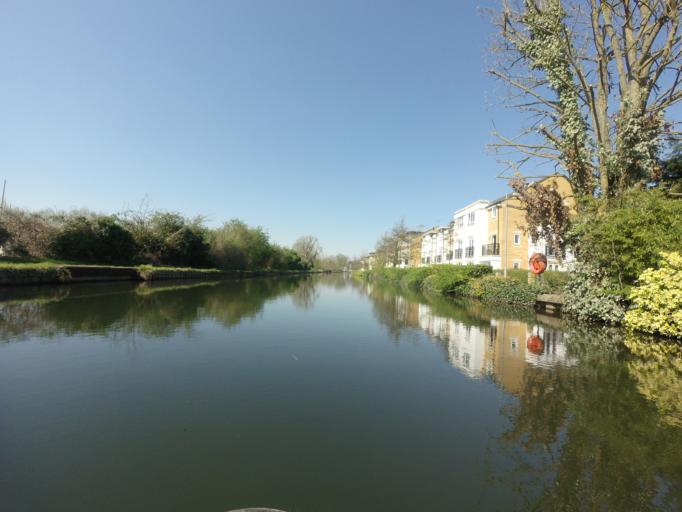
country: GB
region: England
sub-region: Hertfordshire
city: Kings Langley
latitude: 51.7104
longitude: -0.4426
